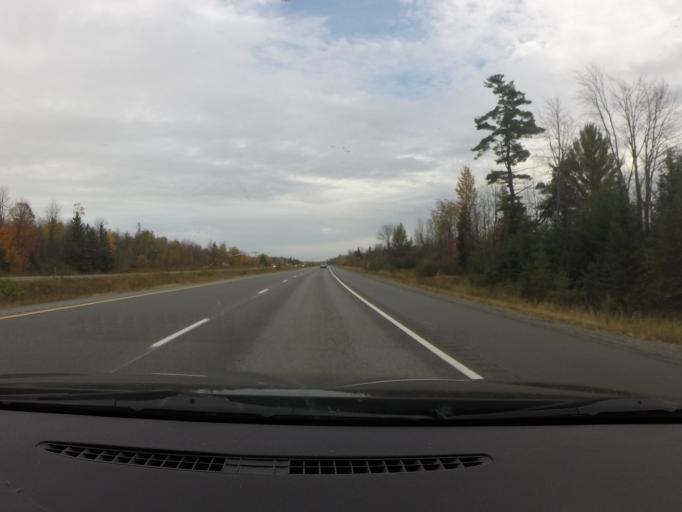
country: CA
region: Ontario
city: Carleton Place
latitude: 45.3075
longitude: -76.0380
